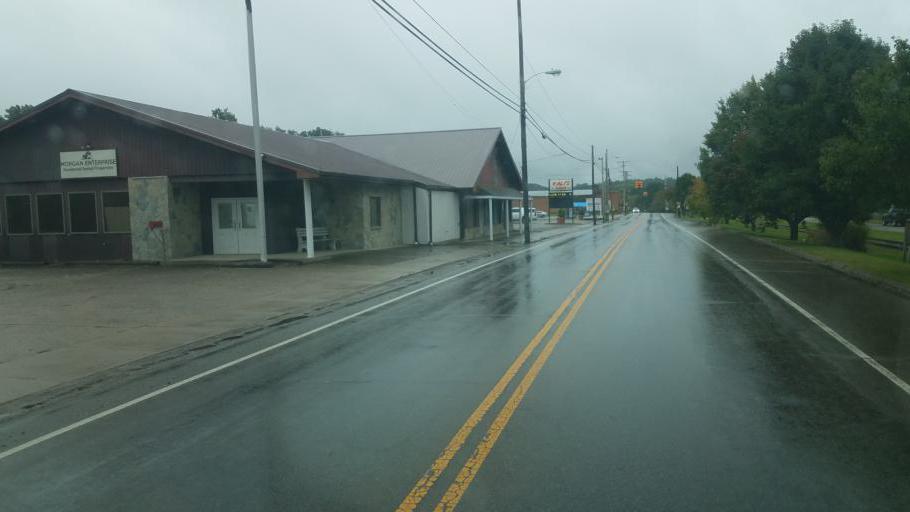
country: US
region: Ohio
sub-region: Jackson County
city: Oak Hill
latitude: 38.8974
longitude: -82.5709
